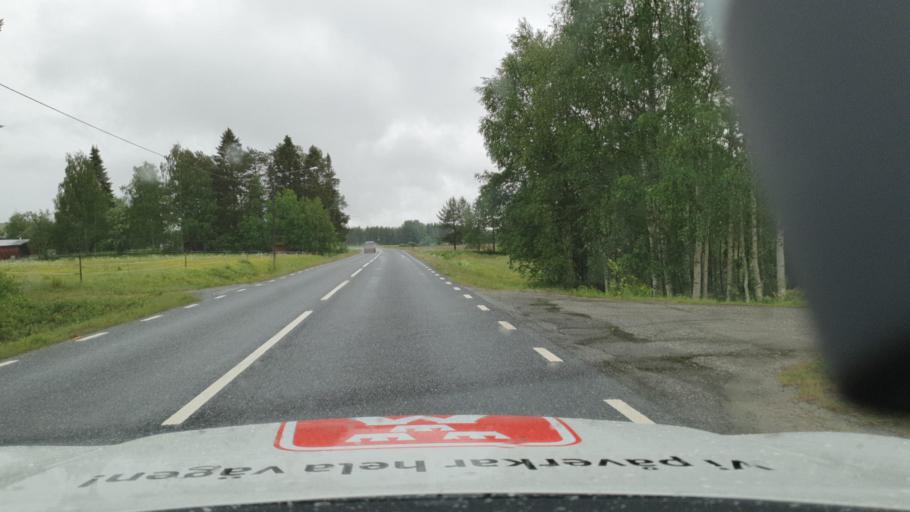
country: SE
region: Vaesterbotten
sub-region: Asele Kommun
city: Asele
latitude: 64.0254
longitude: 17.2964
